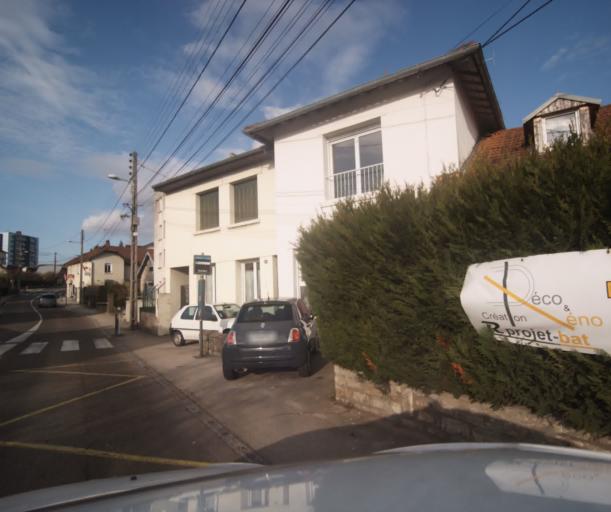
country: FR
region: Franche-Comte
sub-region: Departement du Doubs
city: Besancon
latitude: 47.2550
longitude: 6.0281
